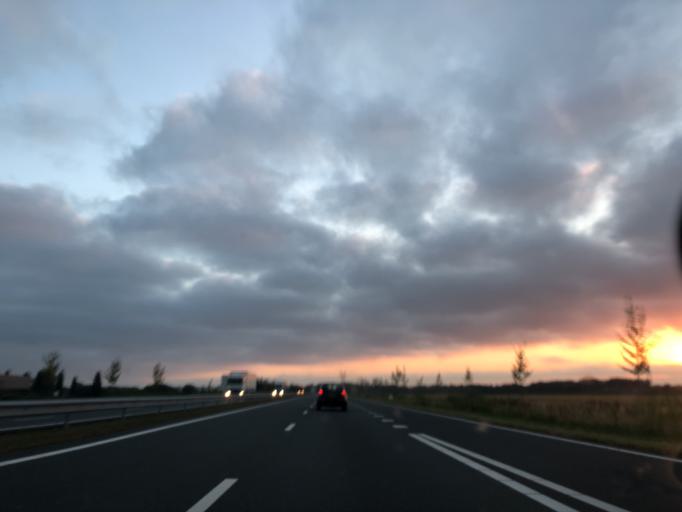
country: NL
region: Groningen
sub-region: Gemeente Veendam
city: Veendam
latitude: 53.0795
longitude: 6.8835
